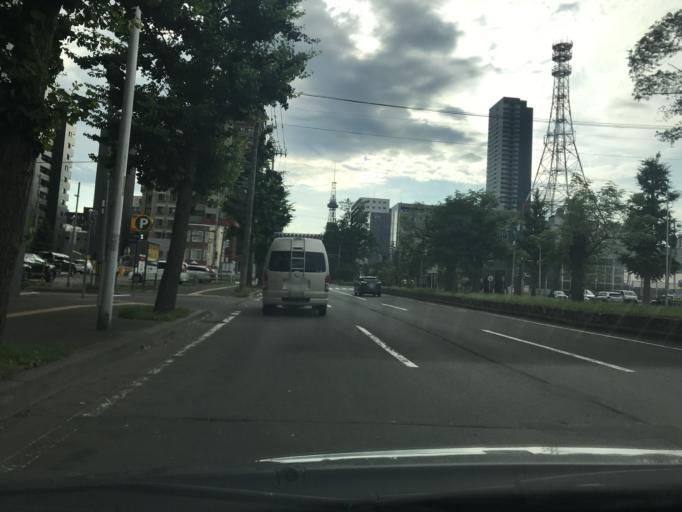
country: JP
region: Hokkaido
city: Sapporo
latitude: 43.0618
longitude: 141.3647
